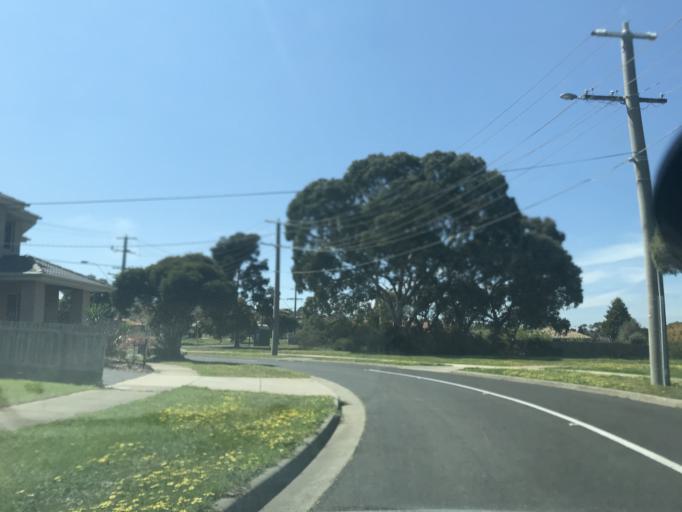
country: AU
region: Victoria
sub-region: Whittlesea
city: Epping
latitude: -37.6399
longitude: 145.0504
